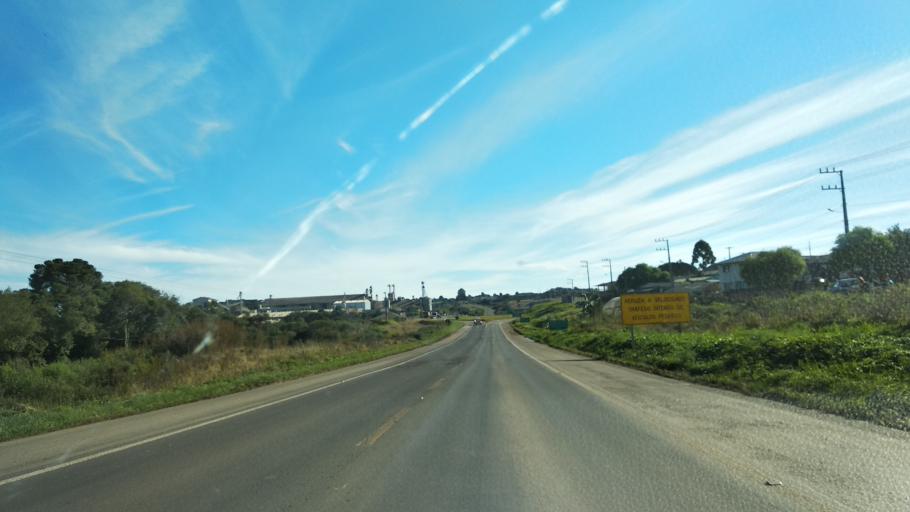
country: BR
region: Santa Catarina
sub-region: Campos Novos
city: Campos Novos
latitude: -27.4080
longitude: -51.2112
